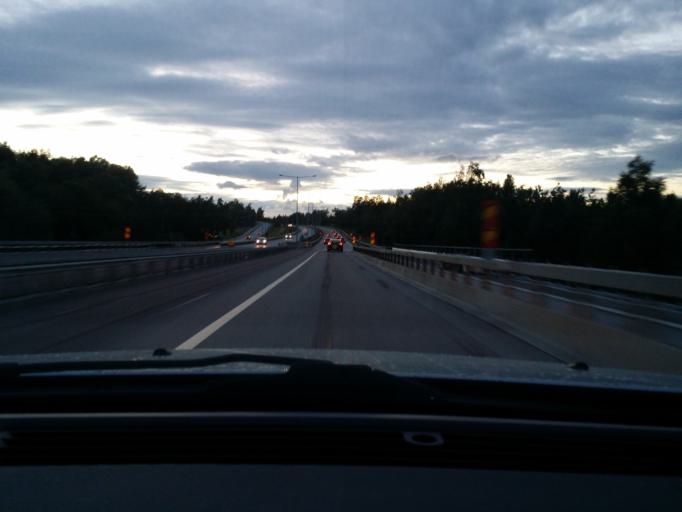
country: SE
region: Stockholm
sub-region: Upplands-Bro Kommun
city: Kungsaengen
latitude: 59.4795
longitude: 17.7870
